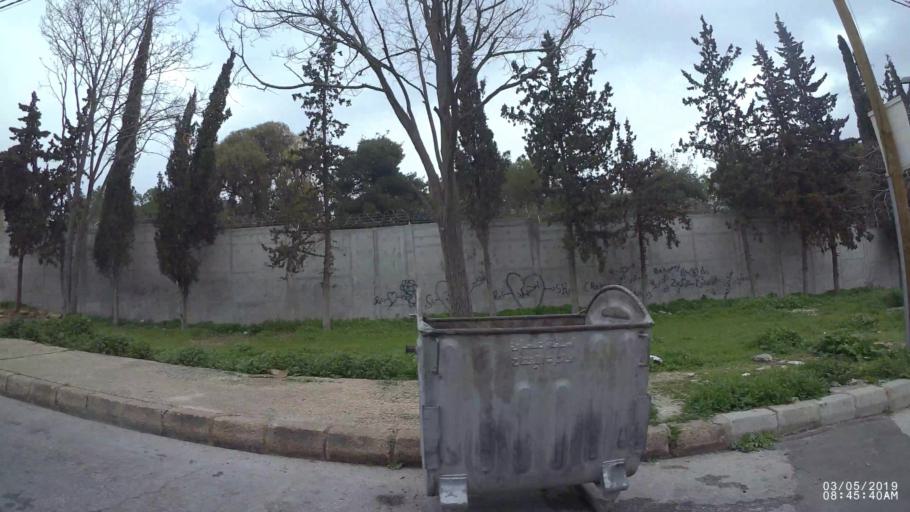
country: JO
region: Amman
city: Amman
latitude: 31.9594
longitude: 35.9432
